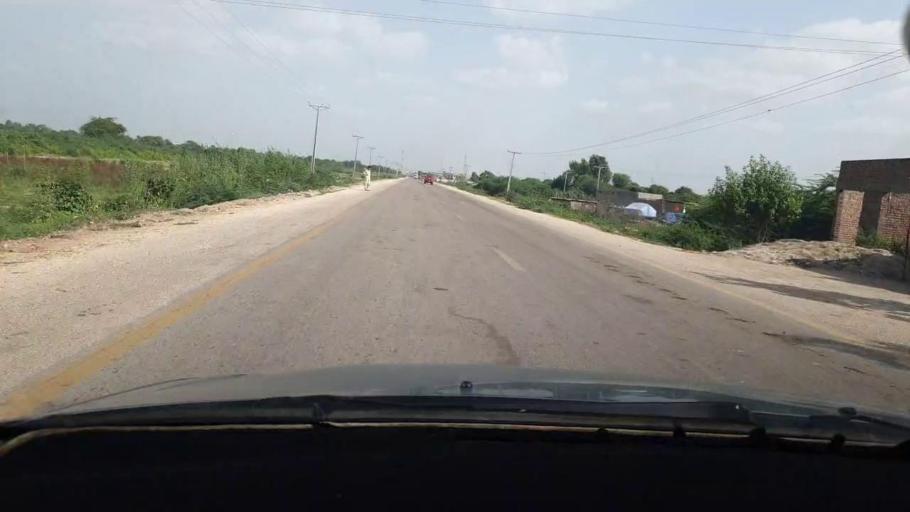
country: PK
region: Sindh
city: Naukot
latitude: 24.8636
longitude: 69.3876
